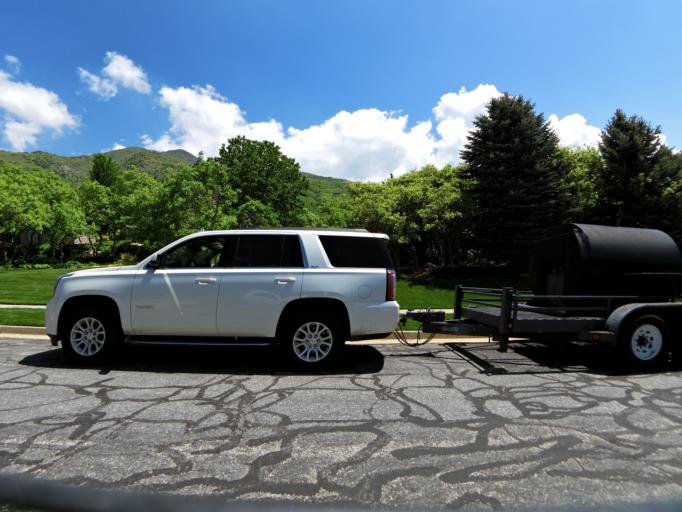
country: US
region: Utah
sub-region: Weber County
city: Uintah
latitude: 41.1613
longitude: -111.9215
